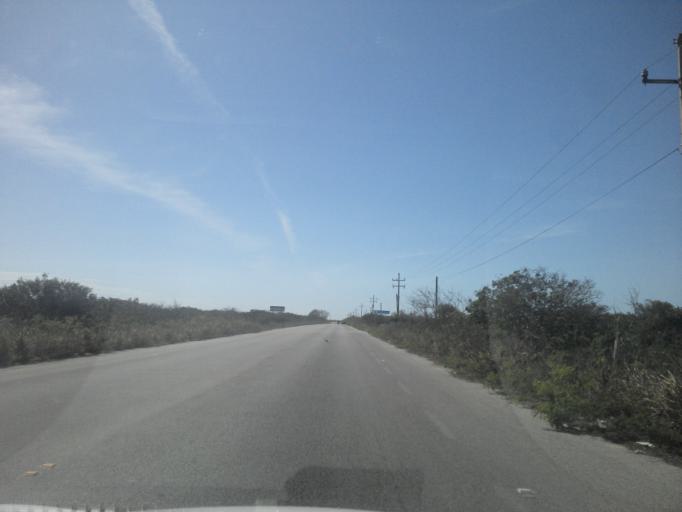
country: MX
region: Yucatan
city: Telchac Puerto
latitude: 21.3324
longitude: -89.3547
